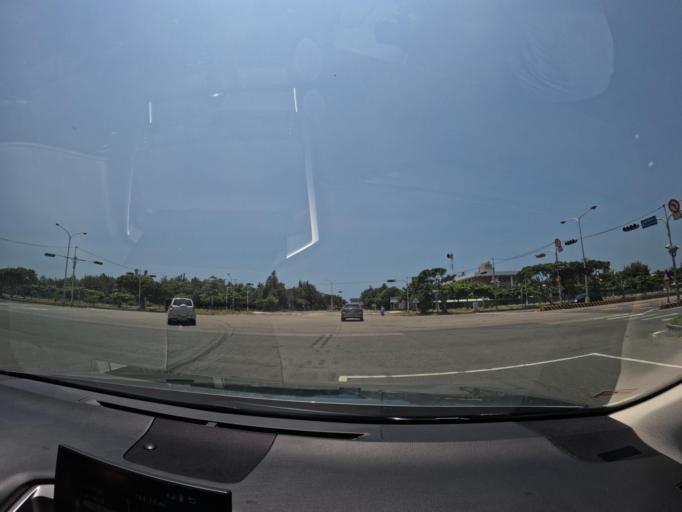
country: TW
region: Taiwan
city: Fengyuan
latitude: 24.2616
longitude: 120.5278
